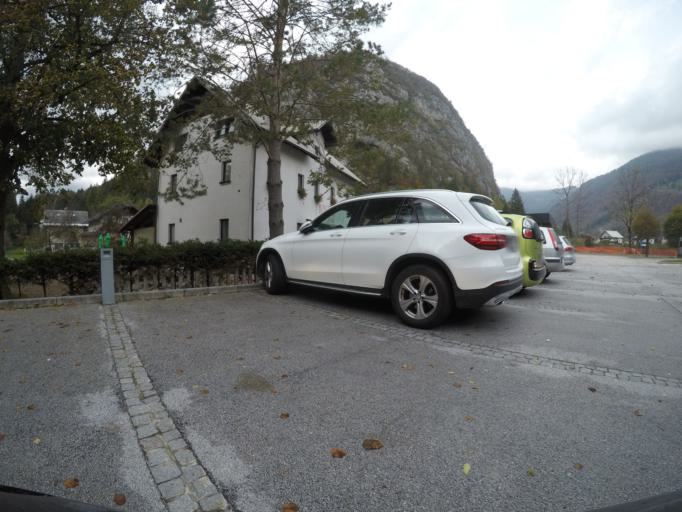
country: SI
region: Kranjska Gora
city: Mojstrana
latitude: 46.4598
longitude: 13.9379
